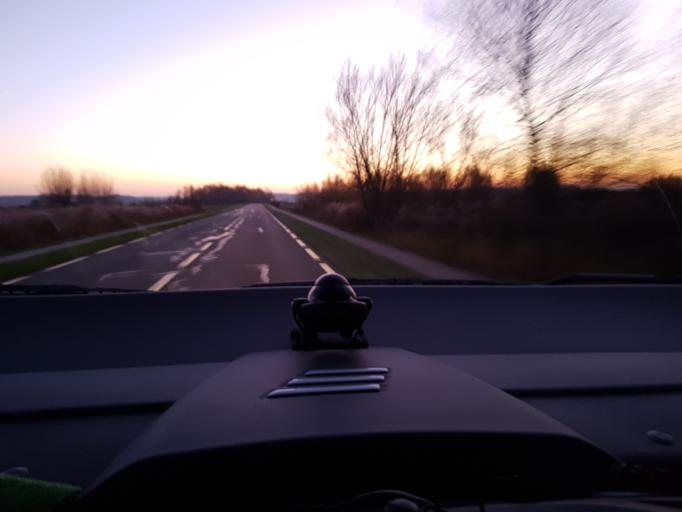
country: FR
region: Picardie
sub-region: Departement de la Somme
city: Saint-Valery-sur-Somme
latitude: 50.1785
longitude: 1.6903
